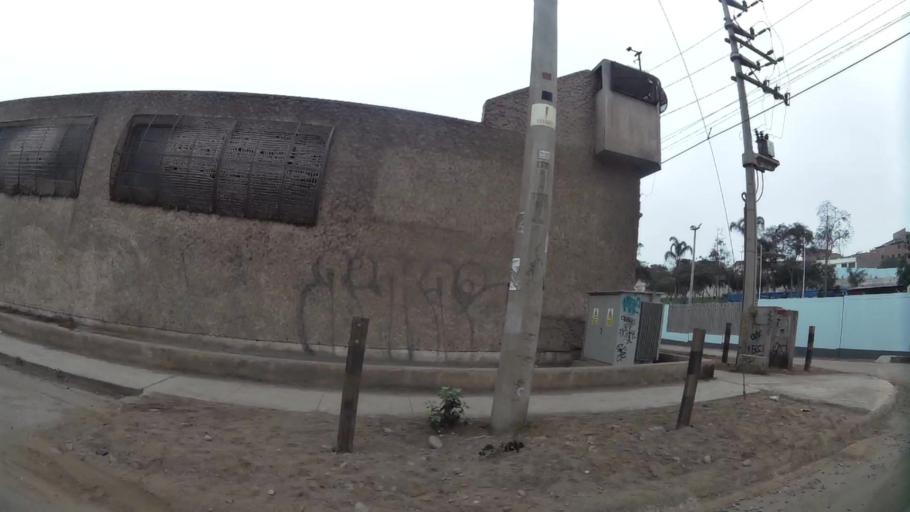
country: PE
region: Lima
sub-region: Lima
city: Surco
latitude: -12.1577
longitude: -76.9784
